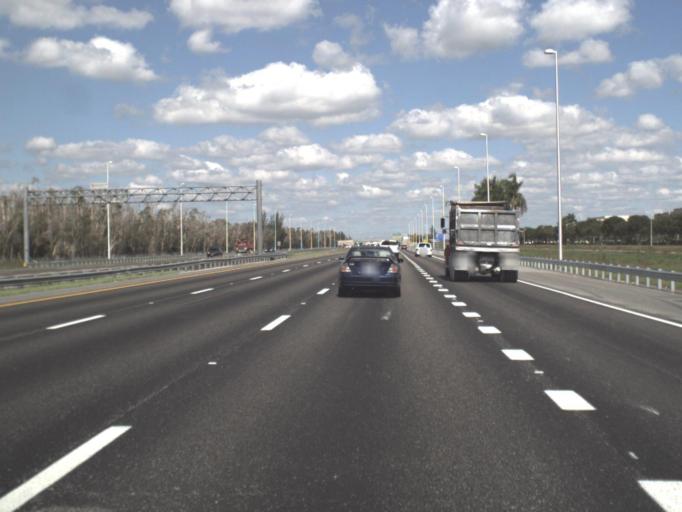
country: US
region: Florida
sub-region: Miami-Dade County
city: Doral
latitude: 25.8589
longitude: -80.3875
